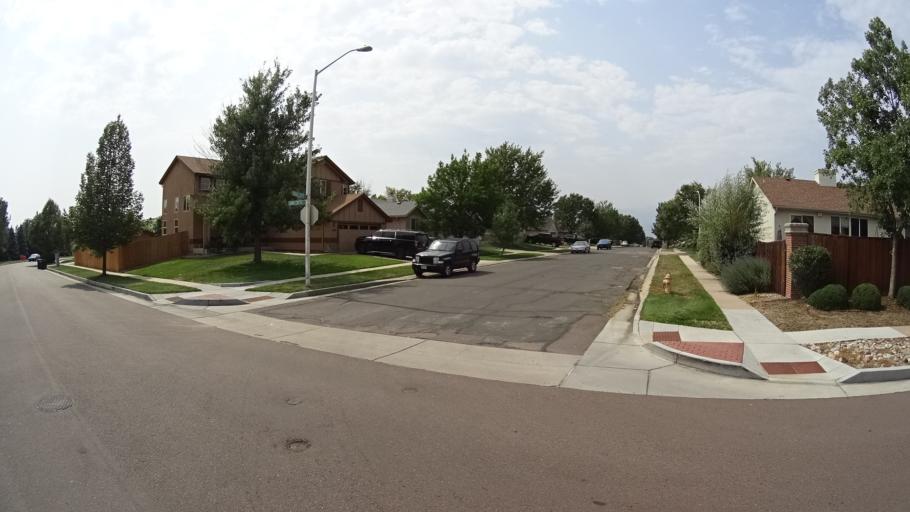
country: US
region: Colorado
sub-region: El Paso County
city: Cimarron Hills
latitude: 38.8239
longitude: -104.7344
